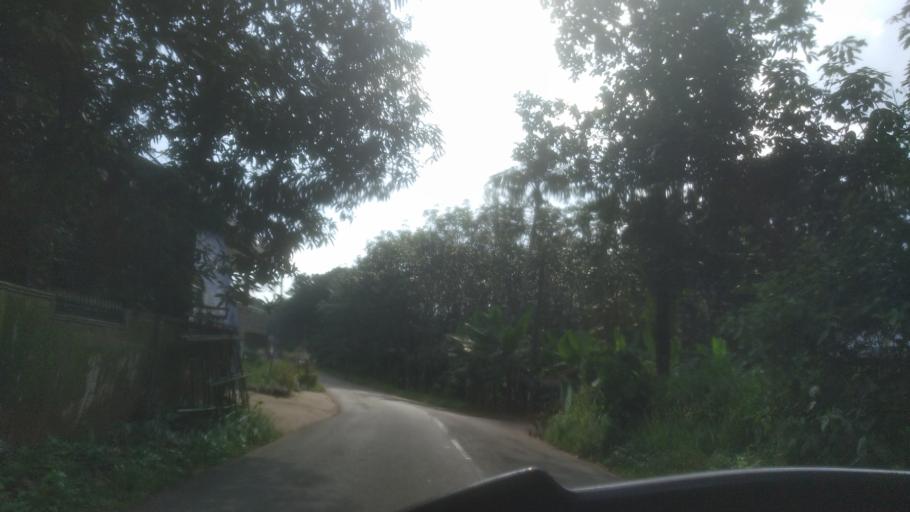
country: IN
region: Kerala
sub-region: Ernakulam
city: Kotamangalam
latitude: 9.9992
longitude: 76.6441
